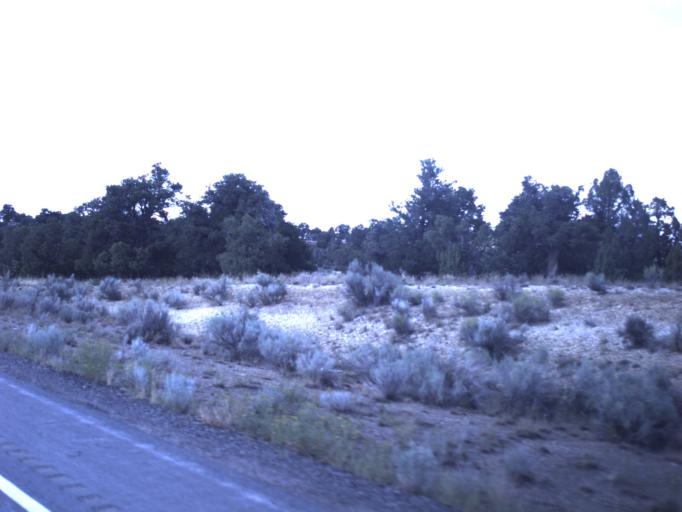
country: US
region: Utah
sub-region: Duchesne County
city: Duchesne
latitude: 40.1766
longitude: -110.5958
